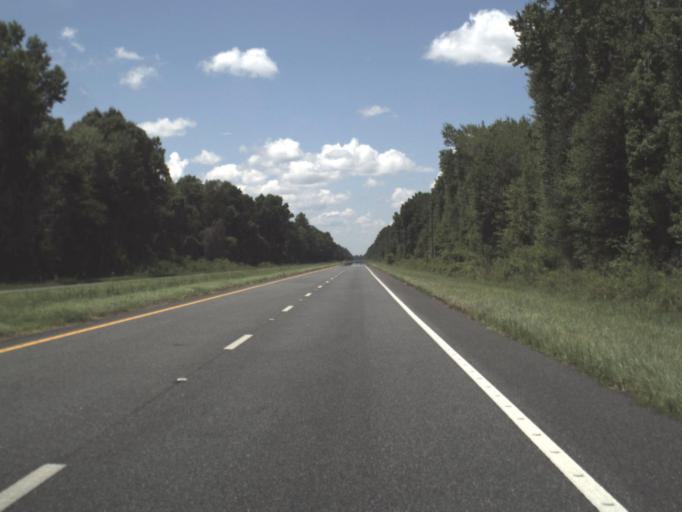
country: US
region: Florida
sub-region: Taylor County
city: Perry
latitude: 30.2877
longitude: -83.7339
